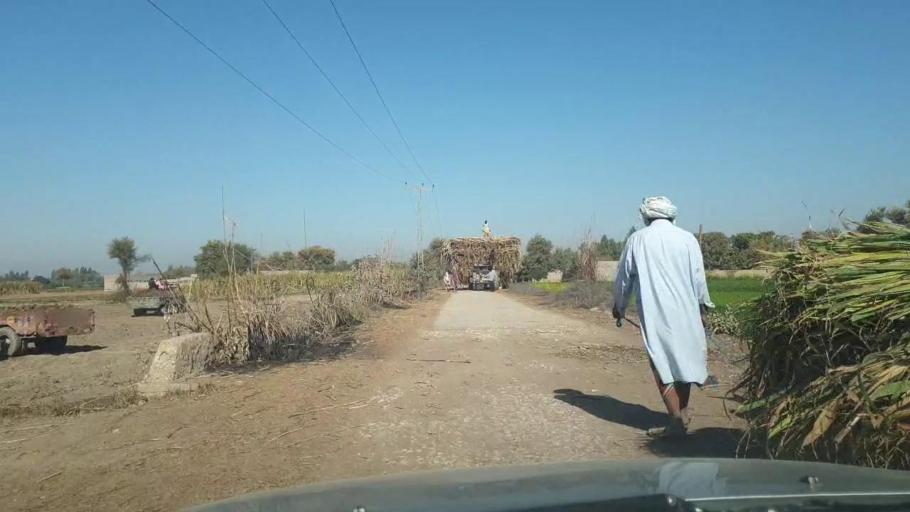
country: PK
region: Sindh
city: Ghotki
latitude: 28.0949
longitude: 69.3428
